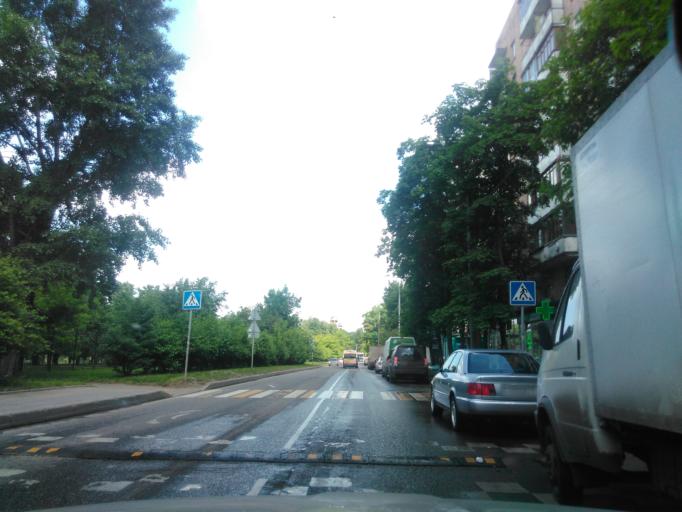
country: RU
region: Moscow
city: Zapadnoye Degunino
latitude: 55.8810
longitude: 37.5330
